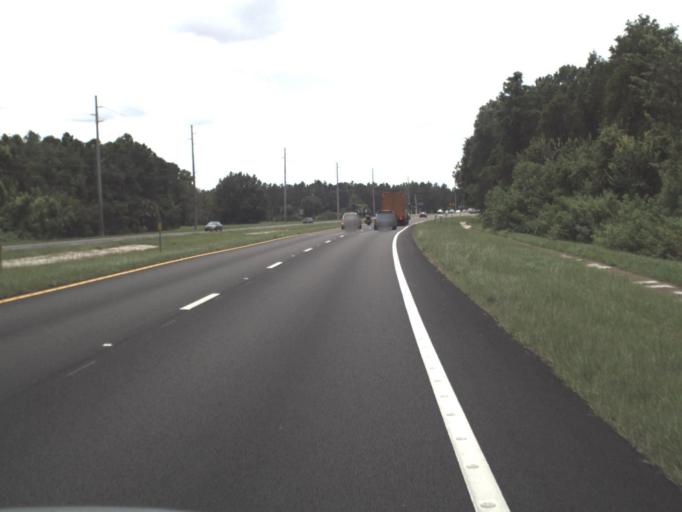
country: US
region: Florida
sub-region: Hillsborough County
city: Lutz
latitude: 28.1612
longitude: -82.4809
